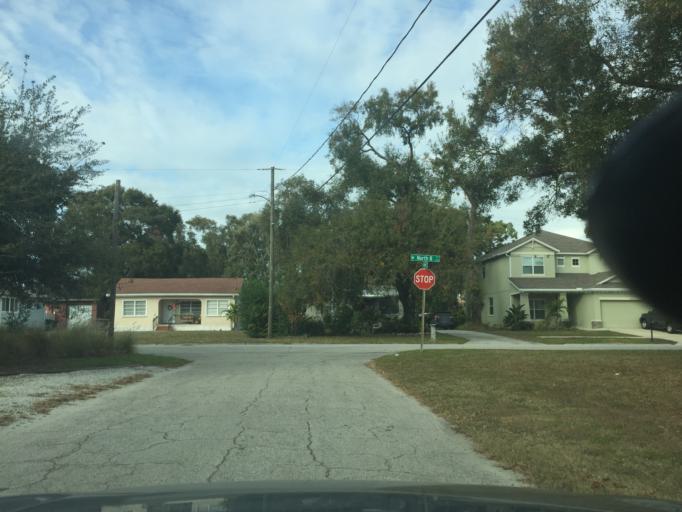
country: US
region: Florida
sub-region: Hillsborough County
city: Tampa
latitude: 27.9470
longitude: -82.4943
